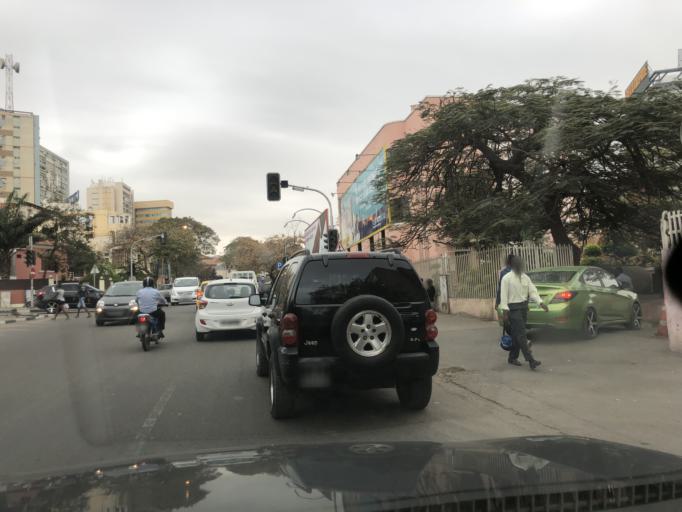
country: AO
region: Luanda
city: Luanda
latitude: -8.8237
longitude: 13.2304
